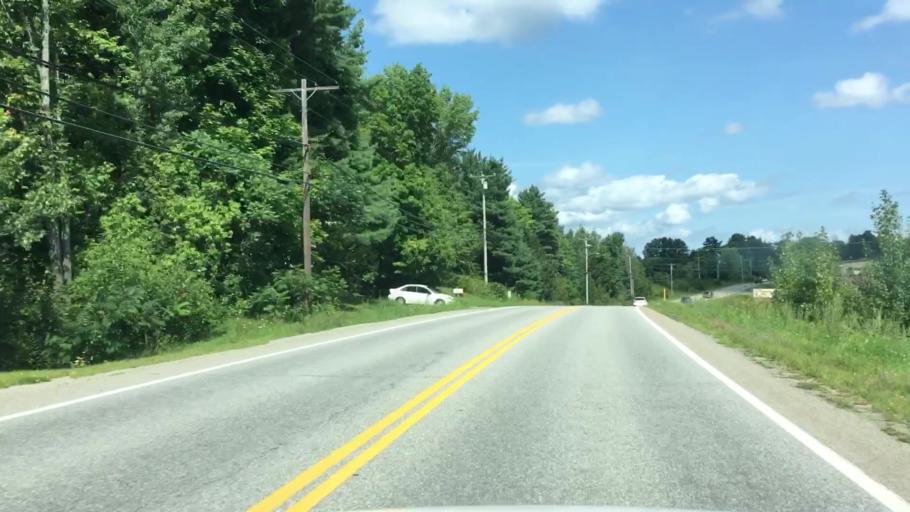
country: US
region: Maine
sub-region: Kennebec County
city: Augusta
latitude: 44.3240
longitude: -69.8174
